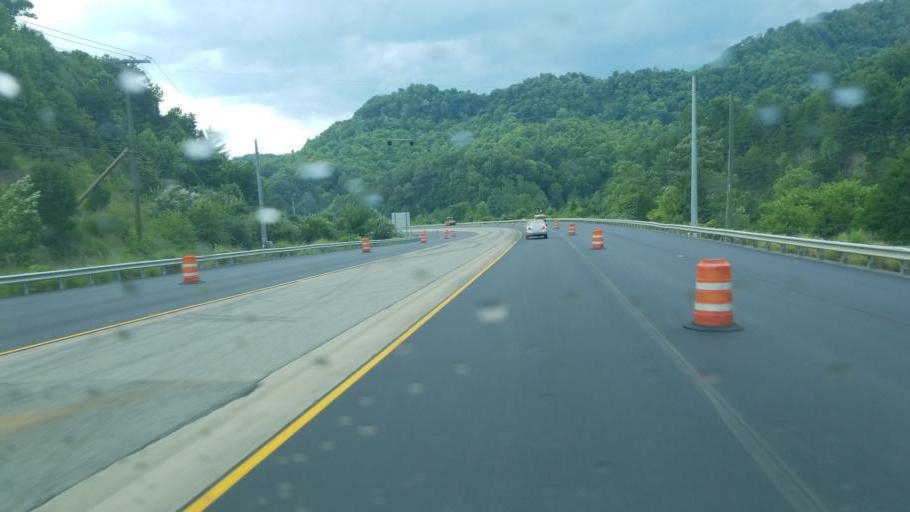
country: US
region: Kentucky
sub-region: Pike County
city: Pikeville
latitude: 37.5130
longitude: -82.5030
